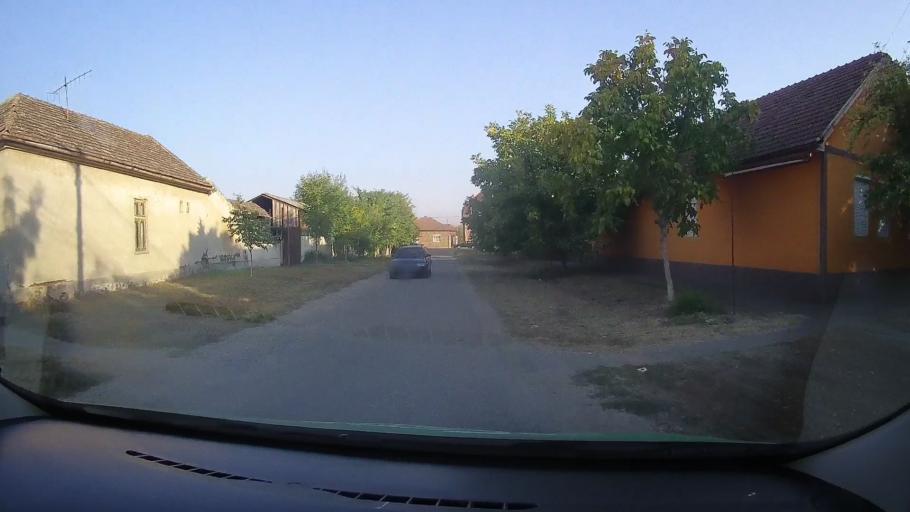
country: RO
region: Arad
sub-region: Comuna Curtici
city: Curtici
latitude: 46.3428
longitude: 21.3117
